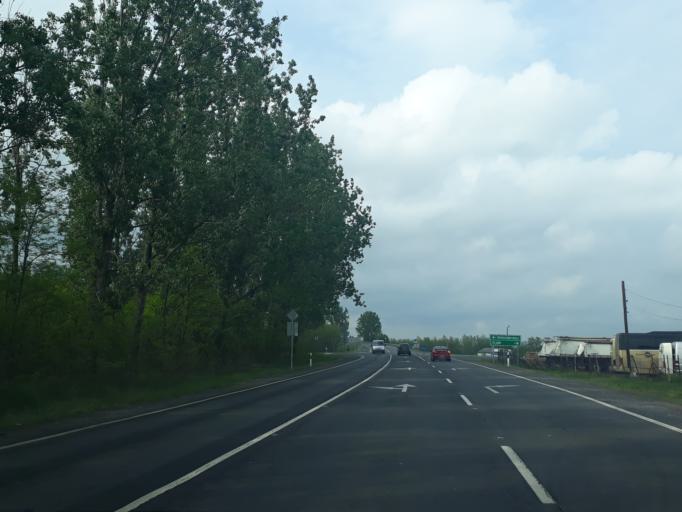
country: HU
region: Szabolcs-Szatmar-Bereg
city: Ajak
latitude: 48.1768
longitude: 22.0411
